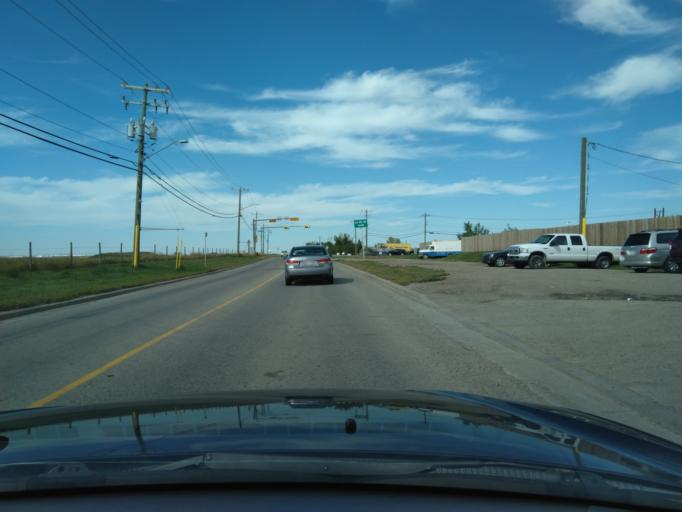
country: CA
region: Alberta
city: Calgary
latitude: 51.1123
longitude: -113.9819
